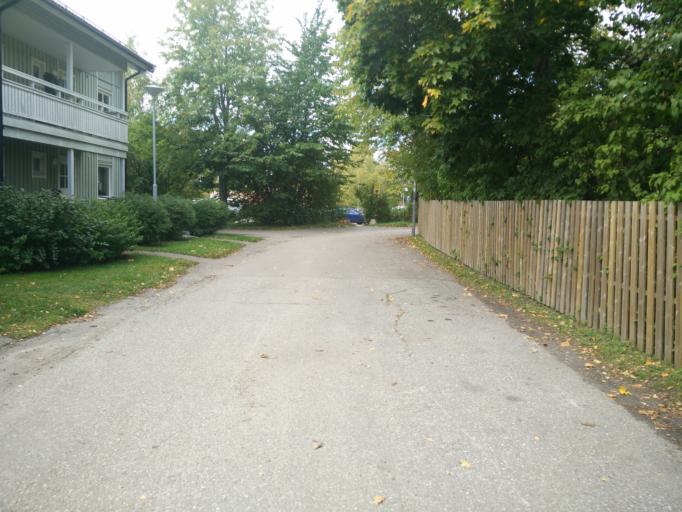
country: SE
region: Vaesternorrland
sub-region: Haernoesands Kommun
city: Haernoesand
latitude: 62.6293
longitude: 17.9466
